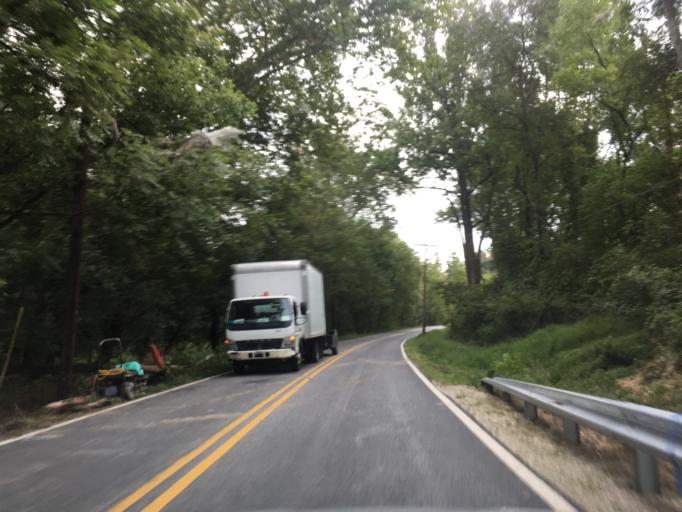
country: US
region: Maryland
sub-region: Baltimore County
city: Hunt Valley
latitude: 39.5217
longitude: -76.6202
